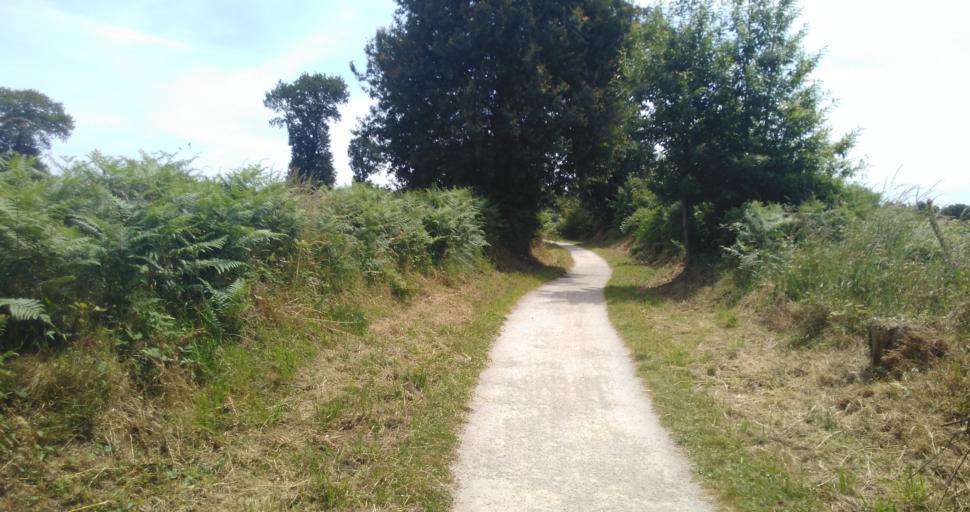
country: FR
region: Brittany
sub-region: Departement d'Ille-et-Vilaine
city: La Meziere
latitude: 48.2195
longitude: -1.7682
